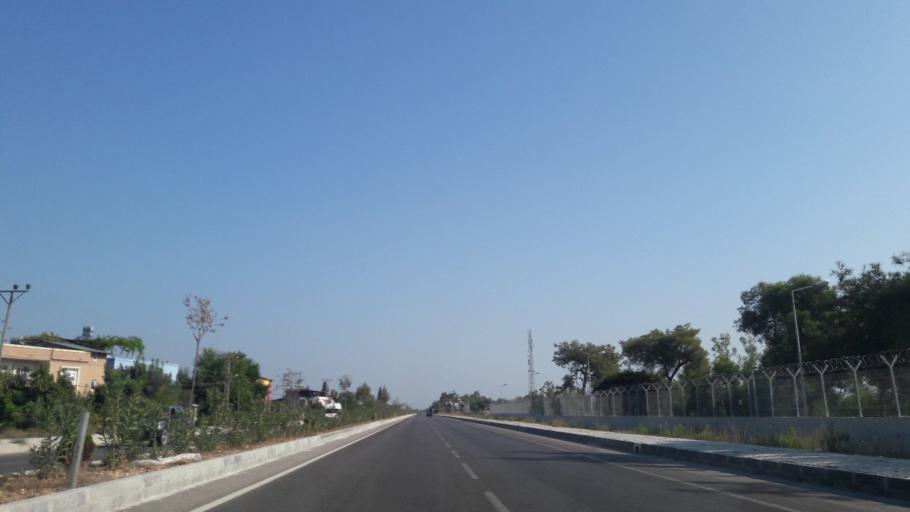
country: TR
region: Adana
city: Yakapinar
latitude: 37.1080
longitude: 35.5100
